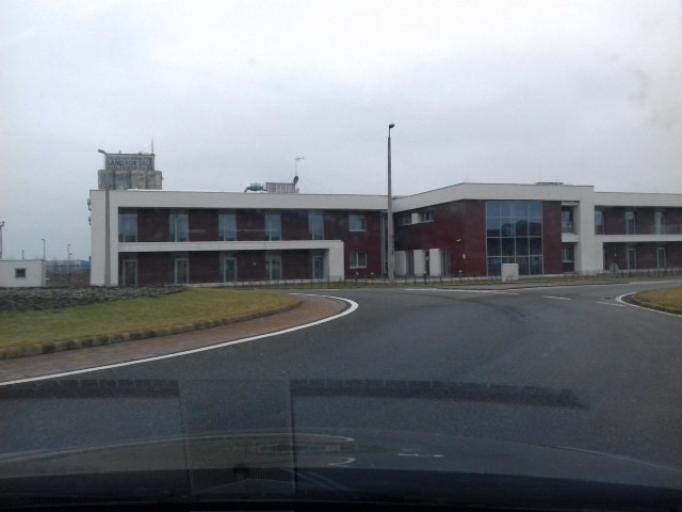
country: HU
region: Hajdu-Bihar
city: Polgar
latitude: 47.8437
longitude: 21.1414
